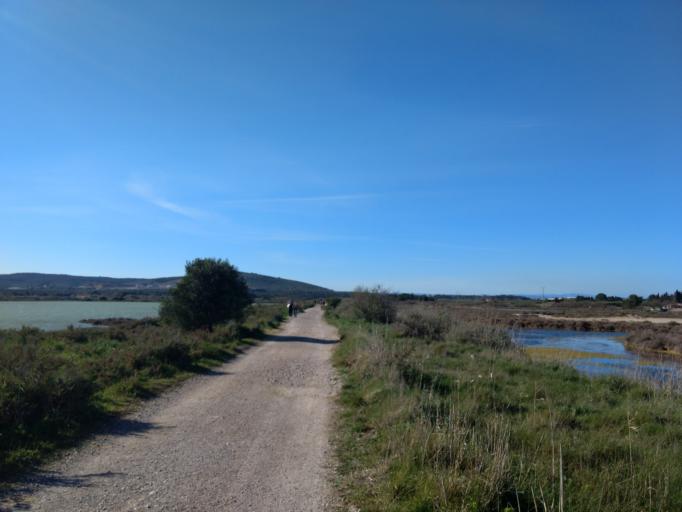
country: FR
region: Languedoc-Roussillon
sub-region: Departement de l'Herault
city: Villeneuve-les-Maguelone
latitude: 43.5195
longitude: 3.8477
